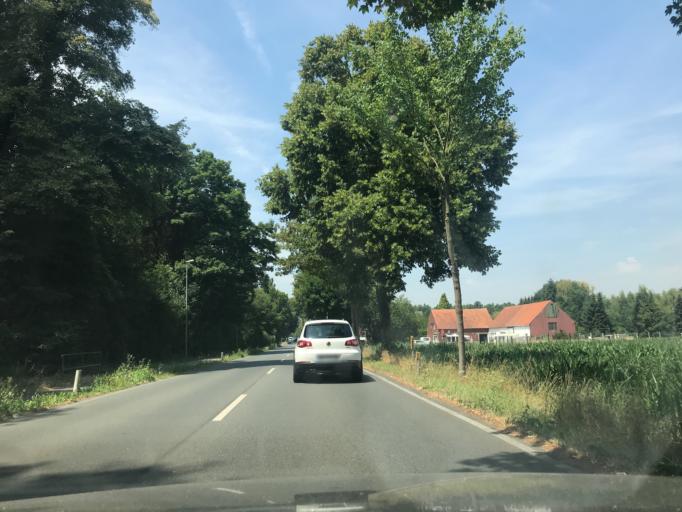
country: DE
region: North Rhine-Westphalia
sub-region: Regierungsbezirk Dusseldorf
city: Wesel
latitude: 51.6829
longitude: 6.5807
